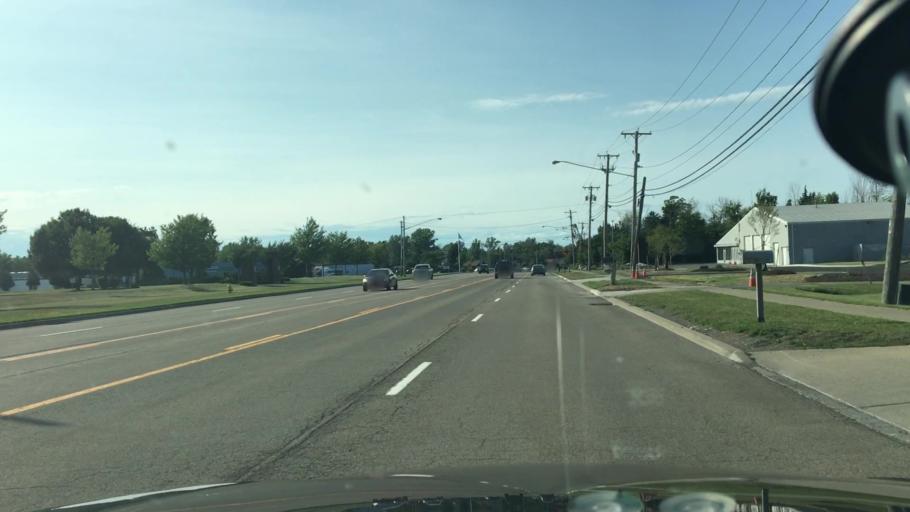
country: US
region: New York
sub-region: Erie County
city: Wanakah
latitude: 42.7555
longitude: -78.8589
